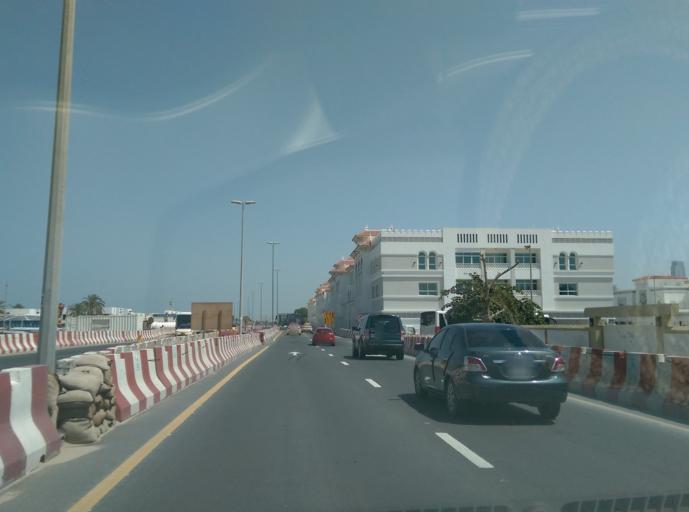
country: AE
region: Dubai
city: Dubai
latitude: 25.1926
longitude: 55.2442
